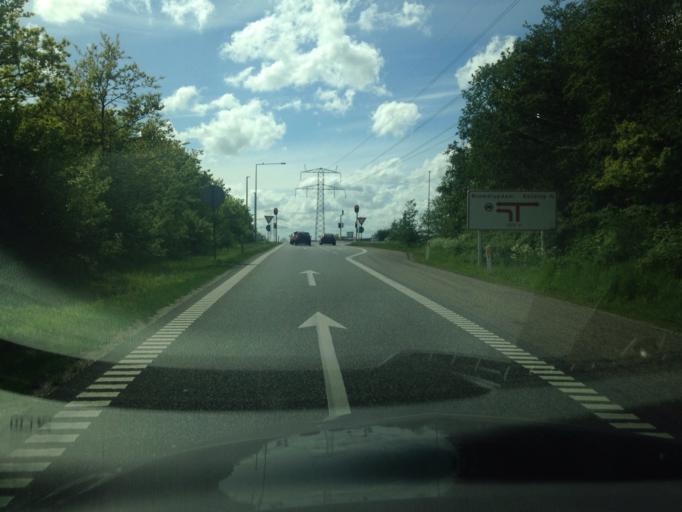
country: DK
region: South Denmark
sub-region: Kolding Kommune
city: Kolding
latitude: 55.5299
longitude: 9.4686
